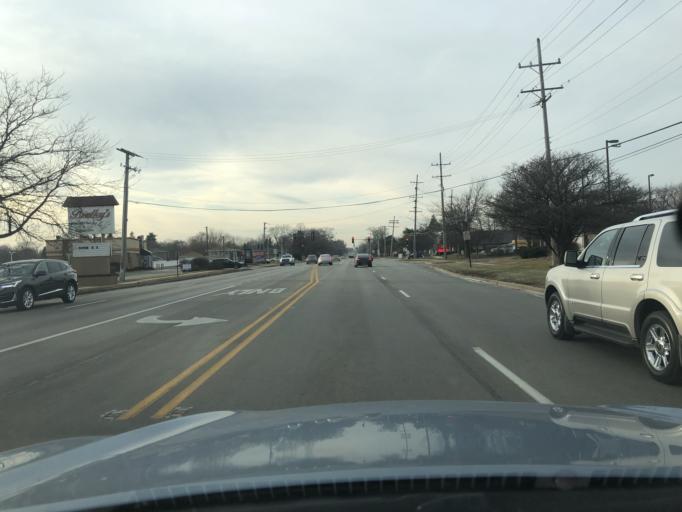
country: US
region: Illinois
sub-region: DuPage County
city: Itasca
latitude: 41.9664
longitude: -87.9966
